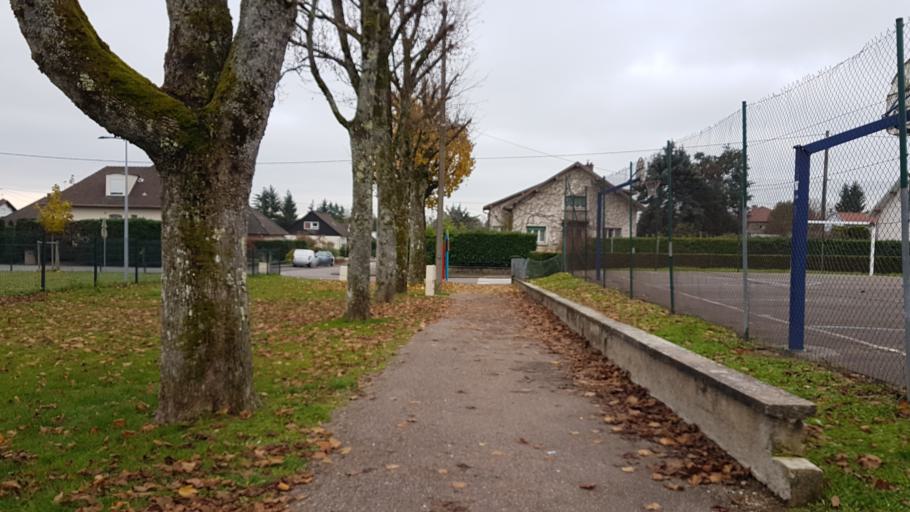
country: FR
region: Franche-Comte
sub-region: Departement de la Haute-Saone
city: Luxeuil-les-Bains
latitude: 47.8131
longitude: 6.3662
